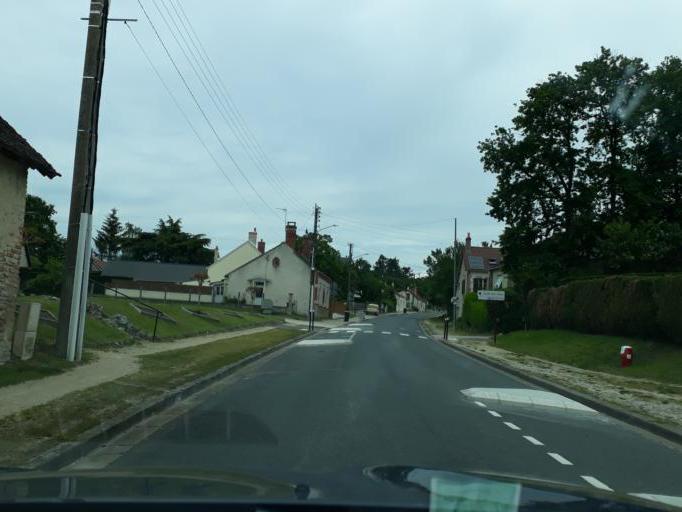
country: FR
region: Centre
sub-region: Departement du Loir-et-Cher
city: Dhuizon
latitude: 47.5898
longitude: 1.6583
